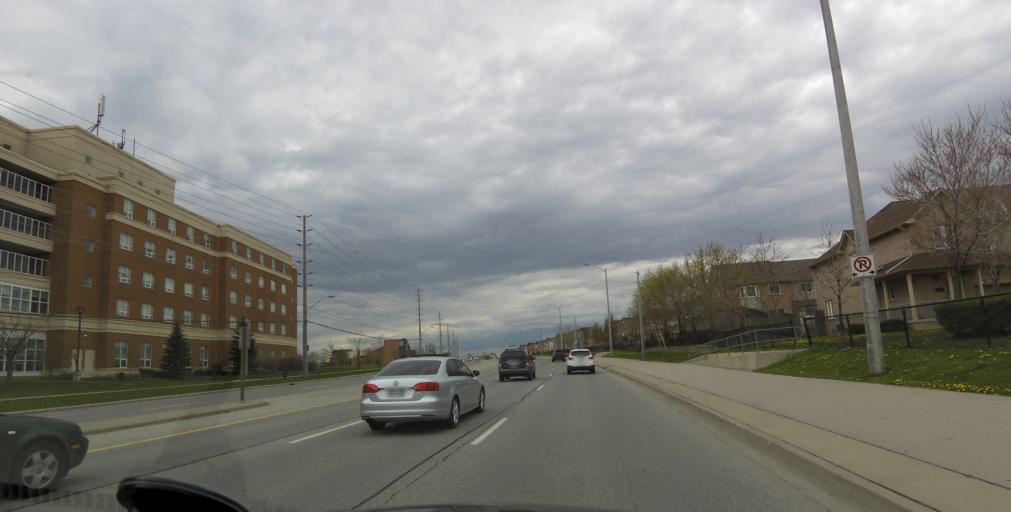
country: CA
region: Ontario
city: Mississauga
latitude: 43.6047
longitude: -79.6862
